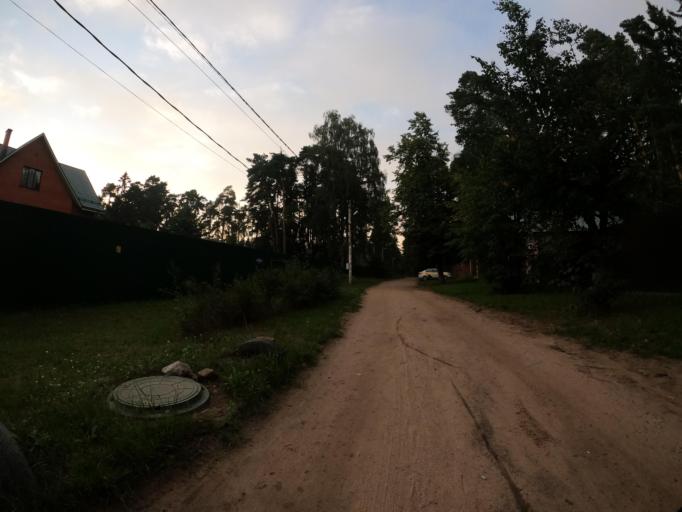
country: RU
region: Moskovskaya
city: Rodniki
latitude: 55.6397
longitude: 38.0652
